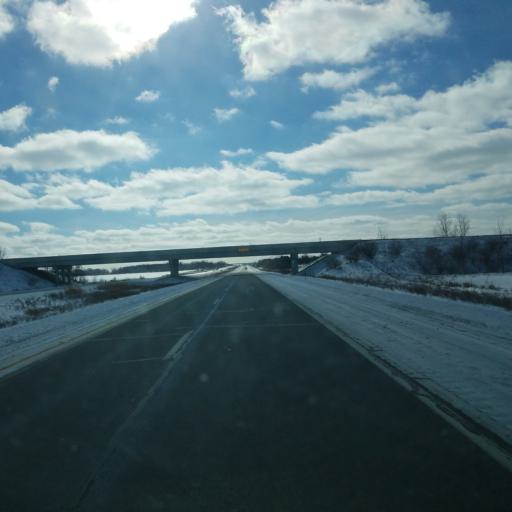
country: US
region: Michigan
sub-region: Clinton County
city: Saint Johns
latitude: 42.9588
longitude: -84.5189
